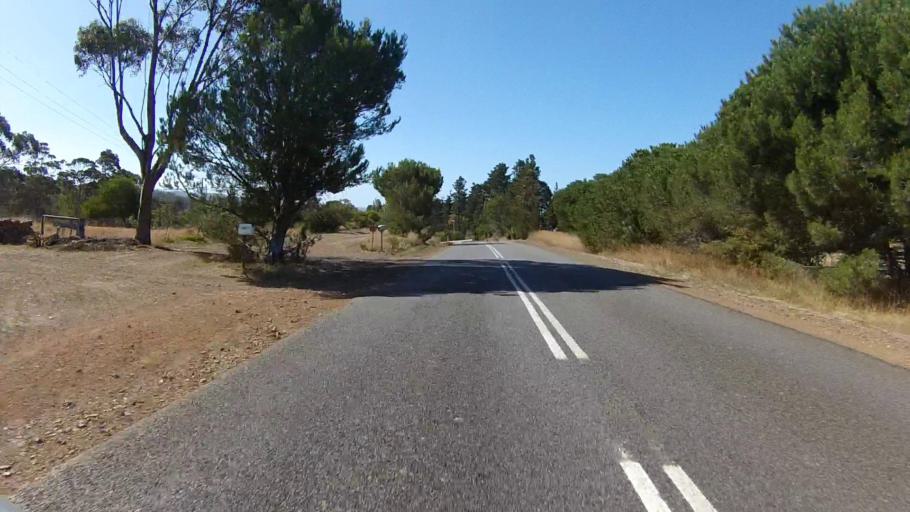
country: AU
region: Tasmania
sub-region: Sorell
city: Sorell
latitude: -42.2875
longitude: 147.9960
